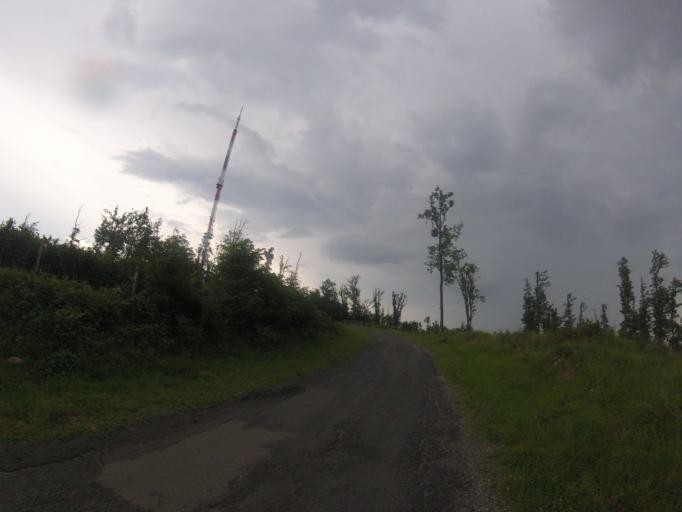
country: HU
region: Veszprem
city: Urkut
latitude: 47.0494
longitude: 17.6500
